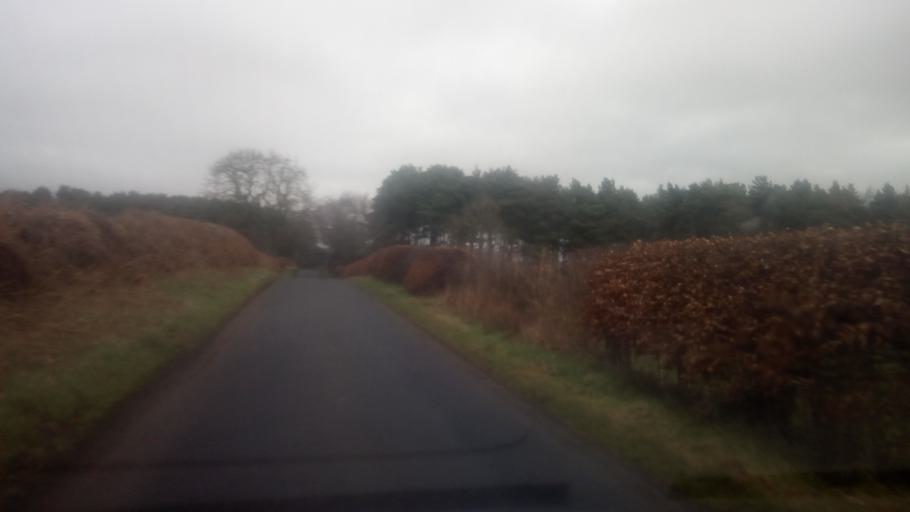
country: GB
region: Scotland
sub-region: The Scottish Borders
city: Kelso
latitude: 55.5418
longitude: -2.4936
